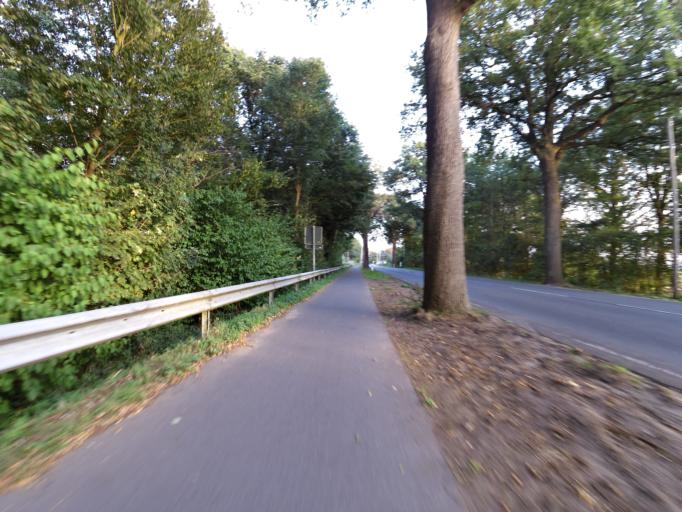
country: NL
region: Gelderland
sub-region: Gemeente Zevenaar
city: Zevenaar
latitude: 51.8949
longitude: 6.1428
